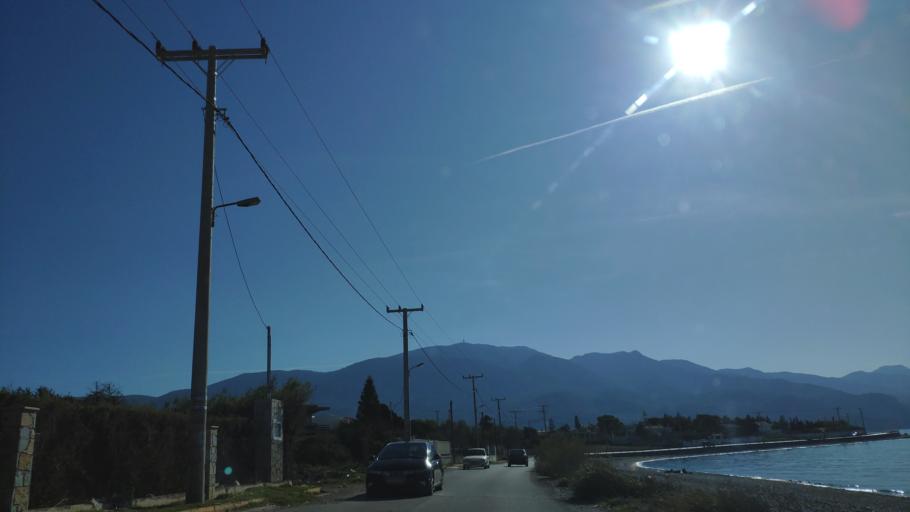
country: GR
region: Attica
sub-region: Nomarchia Dytikis Attikis
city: Kineta
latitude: 38.0883
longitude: 23.1829
